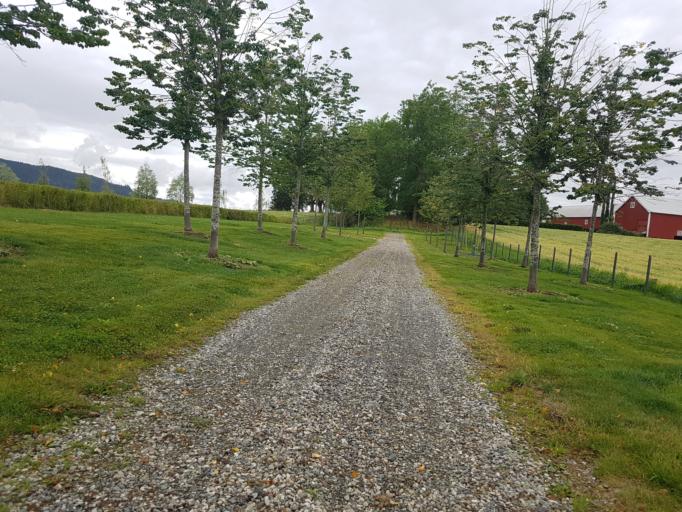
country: NO
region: Sor-Trondelag
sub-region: Trondheim
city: Trondheim
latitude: 63.3817
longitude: 10.4125
